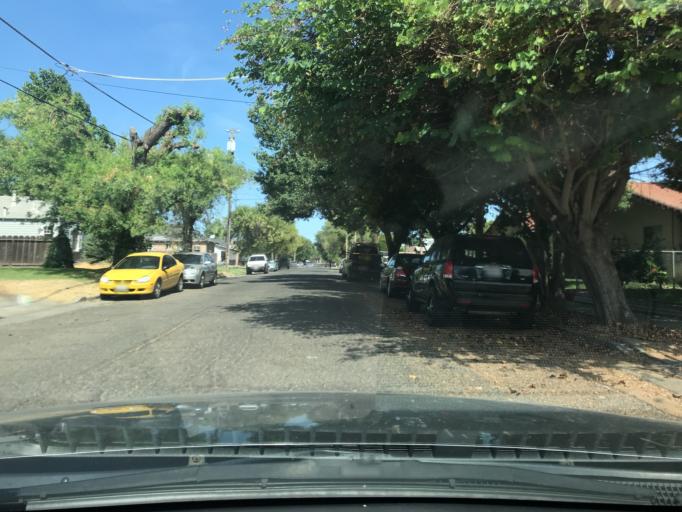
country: US
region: California
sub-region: Merced County
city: Atwater
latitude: 37.3513
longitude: -120.6109
